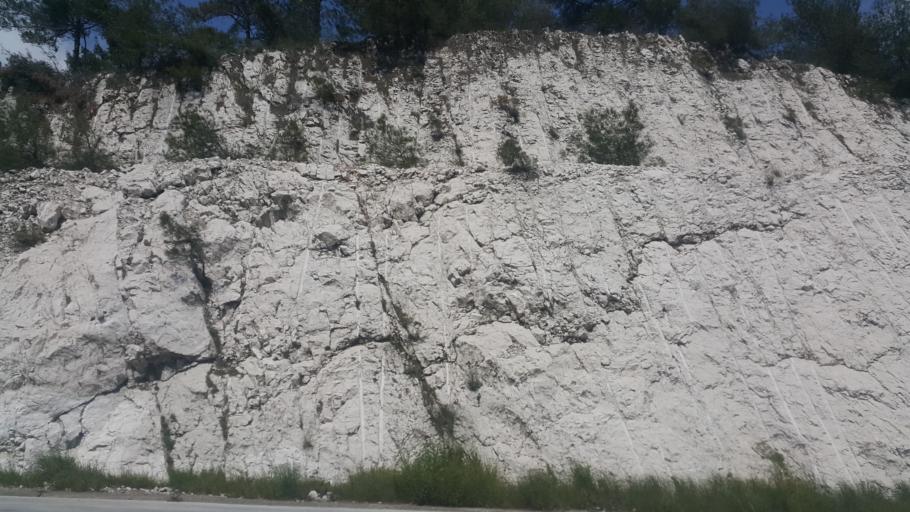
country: TR
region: Mersin
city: Camliyayla
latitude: 37.2084
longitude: 34.8113
